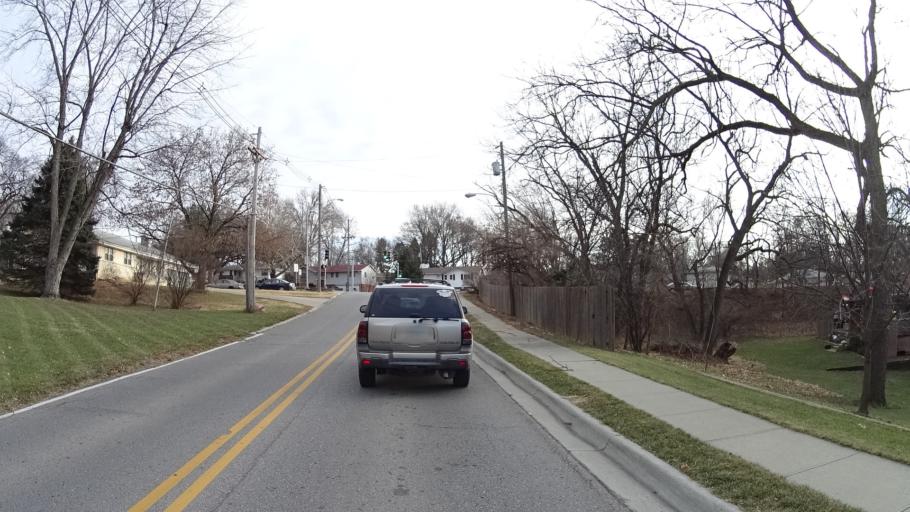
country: US
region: Nebraska
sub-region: Douglas County
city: Ralston
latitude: 41.2349
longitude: -96.0749
